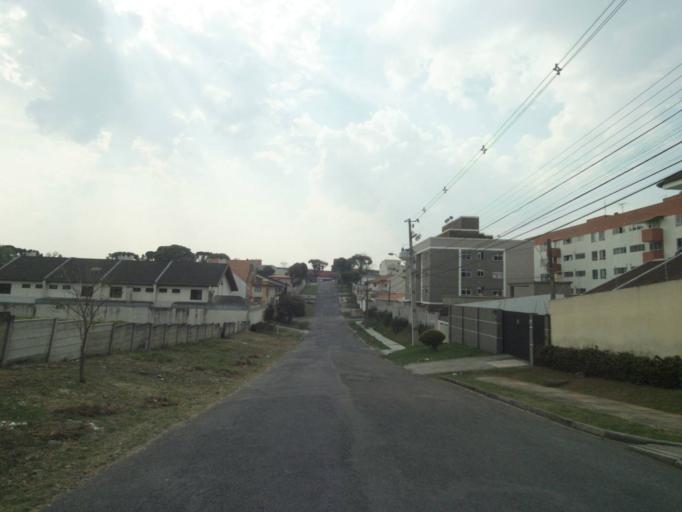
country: BR
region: Parana
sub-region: Curitiba
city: Curitiba
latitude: -25.4607
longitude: -49.2694
